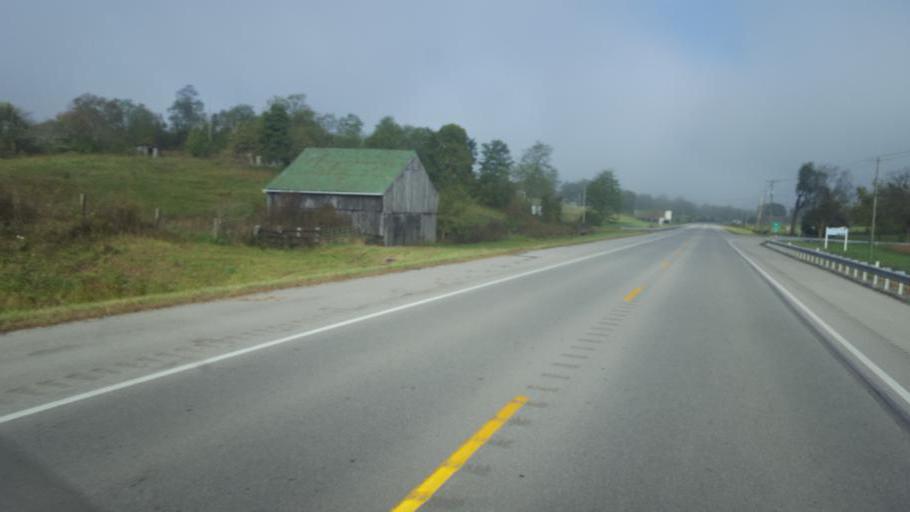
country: US
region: Kentucky
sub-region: Fleming County
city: Flemingsburg
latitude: 38.5304
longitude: -83.7553
